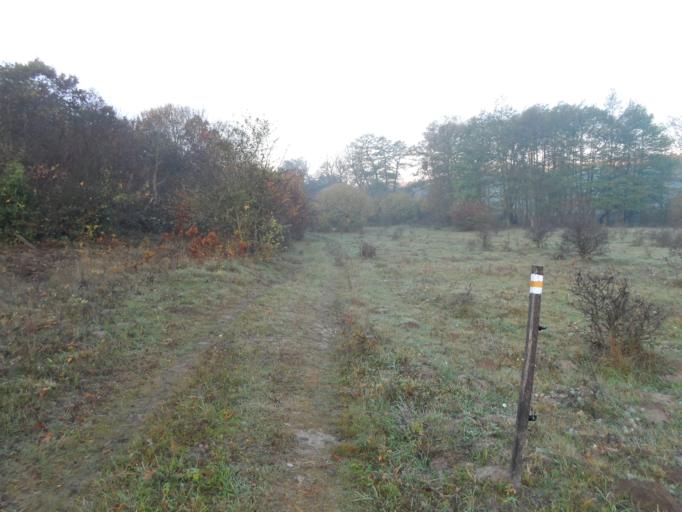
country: HU
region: Veszprem
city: Ajka
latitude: 47.2309
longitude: 17.5727
